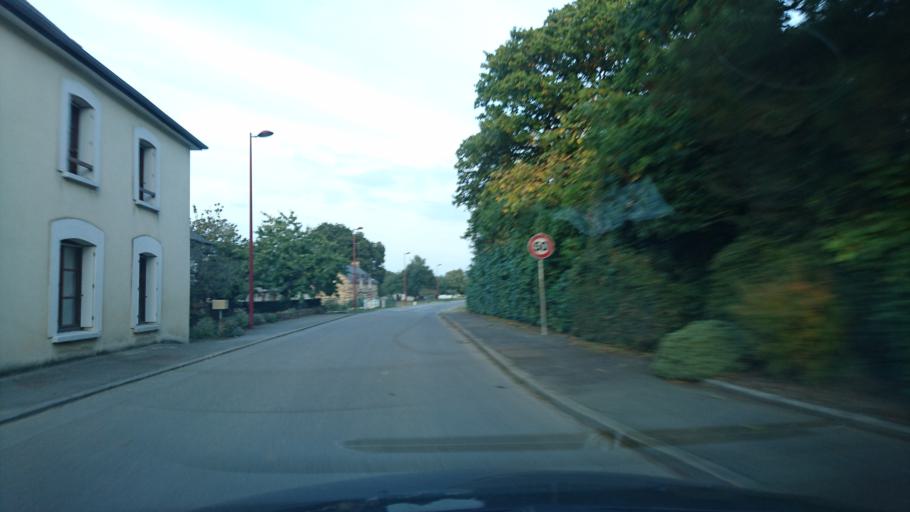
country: FR
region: Brittany
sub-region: Departement d'Ille-et-Vilaine
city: Maure-de-Bretagne
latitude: 47.8895
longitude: -2.0408
